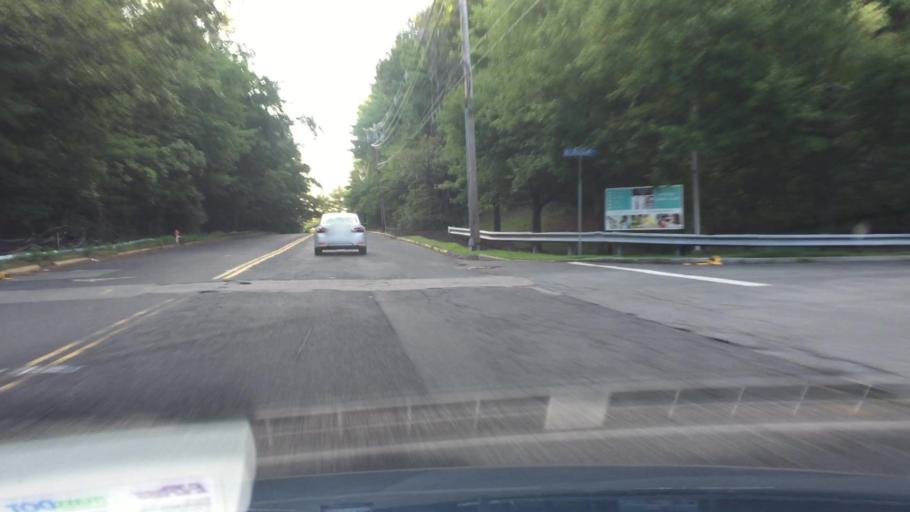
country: US
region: Massachusetts
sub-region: Worcester County
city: Northborough
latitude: 42.3330
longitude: -71.6011
